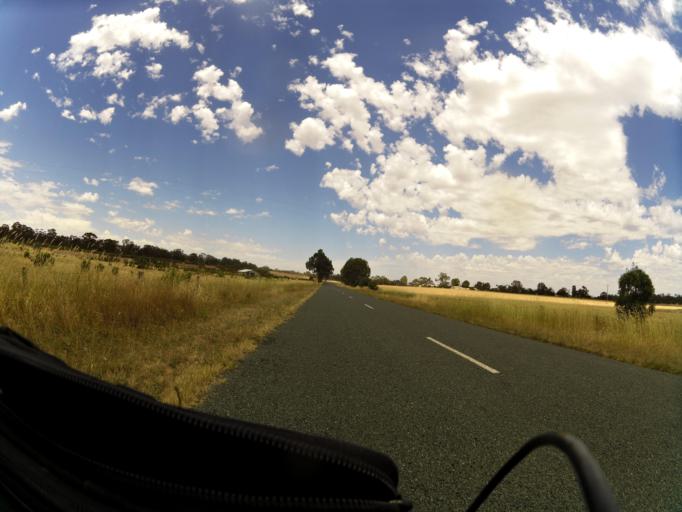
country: AU
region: Victoria
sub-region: Greater Shepparton
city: Shepparton
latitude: -36.6376
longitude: 145.2107
